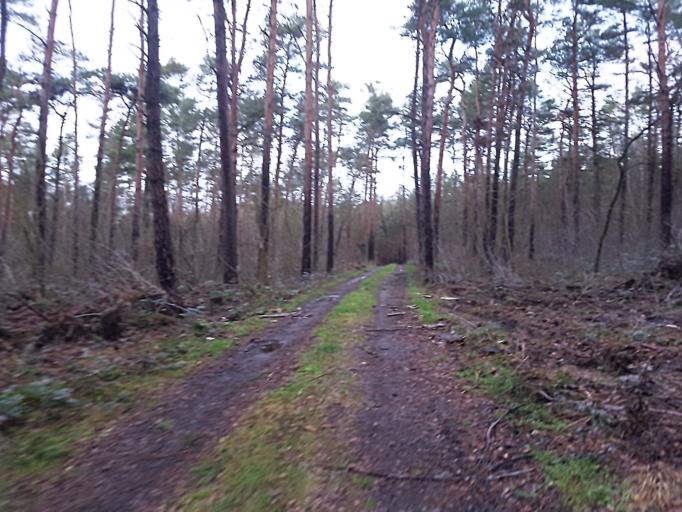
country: DE
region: Brandenburg
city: Schilda
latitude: 51.5829
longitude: 13.3951
